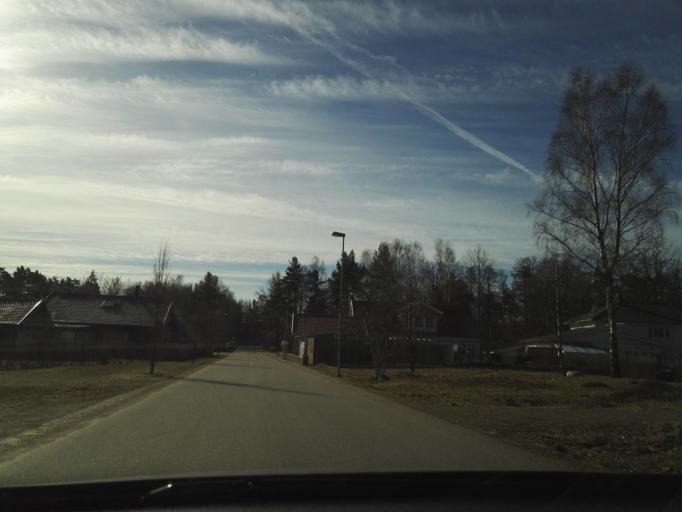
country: SE
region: Kronoberg
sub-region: Vaxjo Kommun
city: Vaexjoe
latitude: 56.9153
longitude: 14.7474
